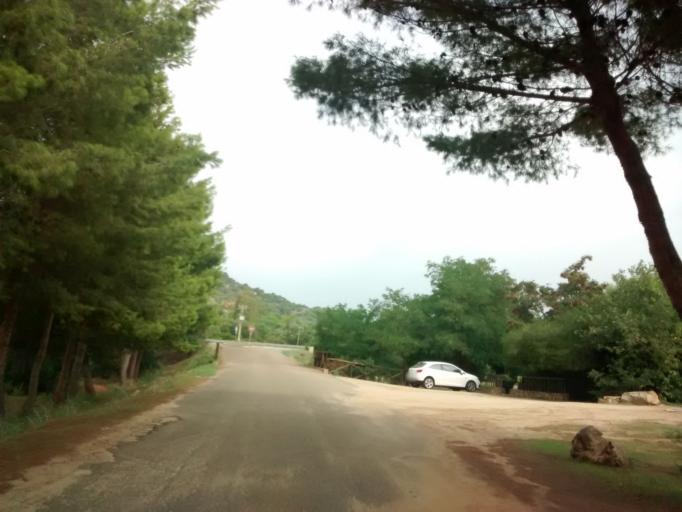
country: IT
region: Sardinia
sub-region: Provincia di Cagliari
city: Villasimius
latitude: 39.1324
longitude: 9.5340
